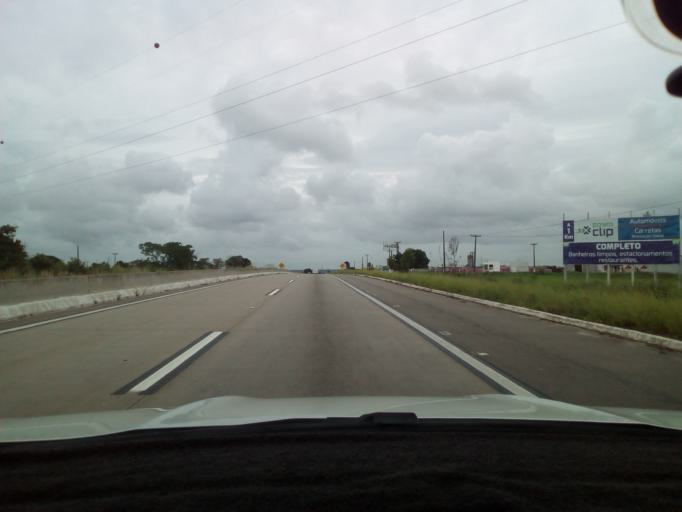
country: BR
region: Paraiba
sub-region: Conde
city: Conde
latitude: -7.2857
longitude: -34.9388
